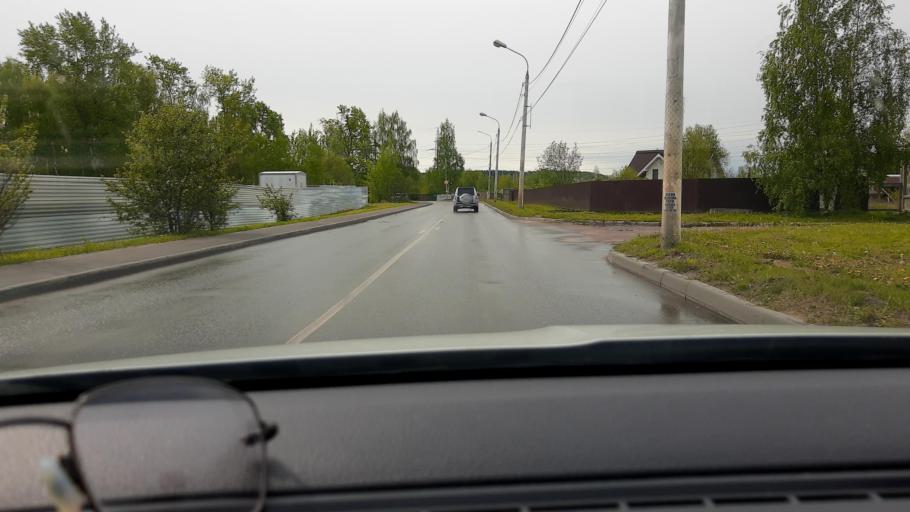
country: RU
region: Moskovskaya
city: Nakhabino
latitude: 55.8368
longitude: 37.1496
